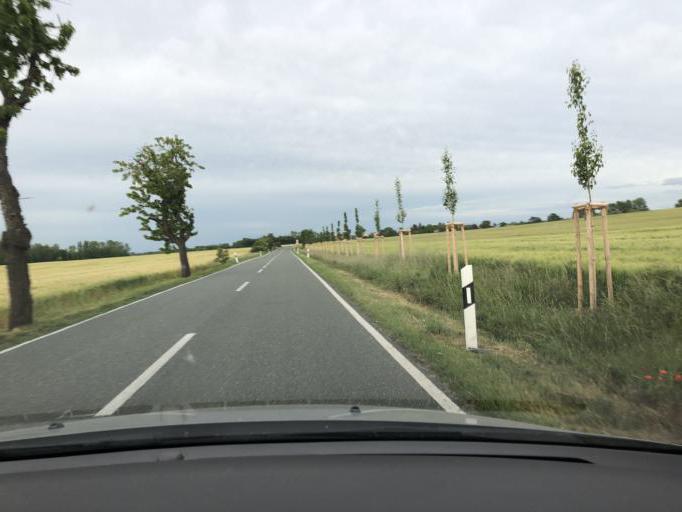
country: DE
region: Thuringia
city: Kleinobringen
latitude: 51.0335
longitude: 11.3208
